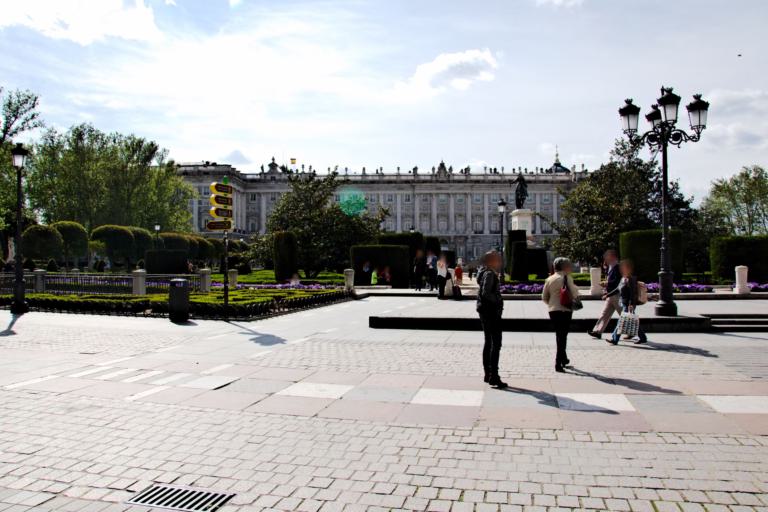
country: ES
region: Madrid
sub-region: Provincia de Madrid
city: City Center
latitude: 40.4182
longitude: -3.7123
